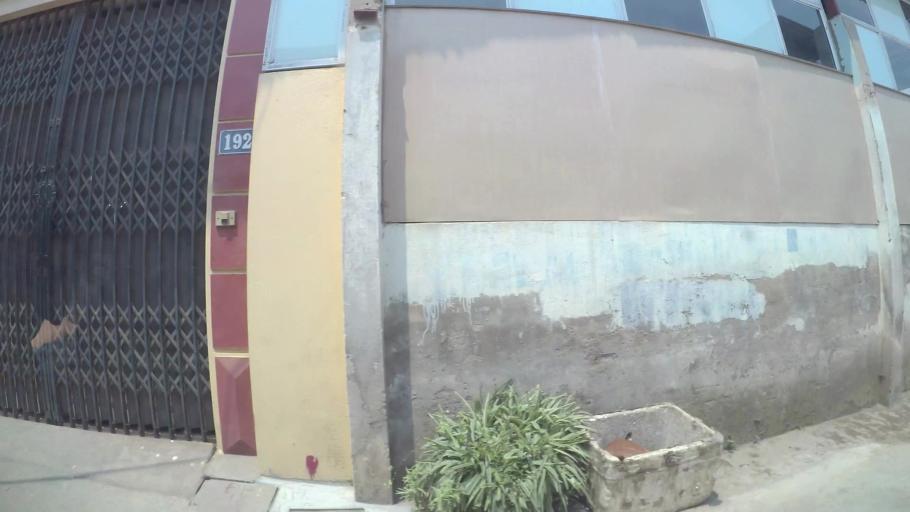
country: VN
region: Ha Noi
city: Van Dien
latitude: 20.9535
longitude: 105.8252
